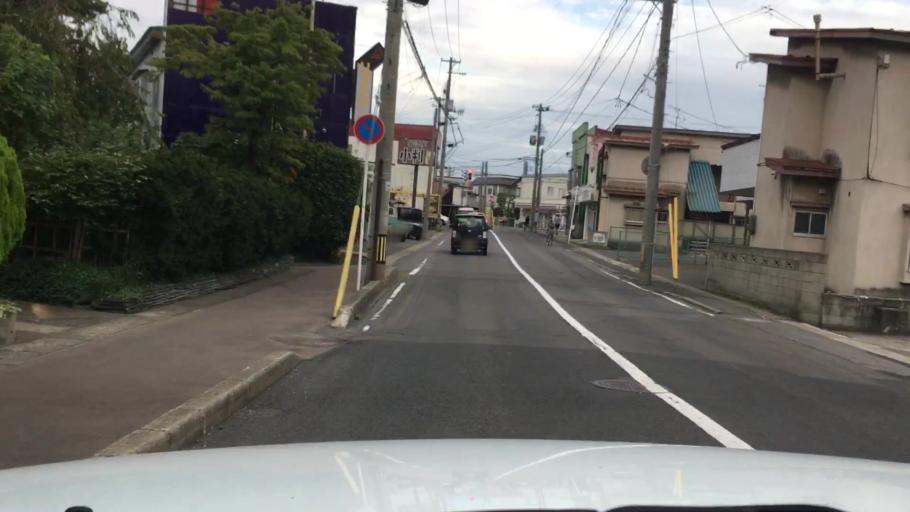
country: JP
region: Aomori
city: Hirosaki
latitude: 40.5853
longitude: 140.4702
